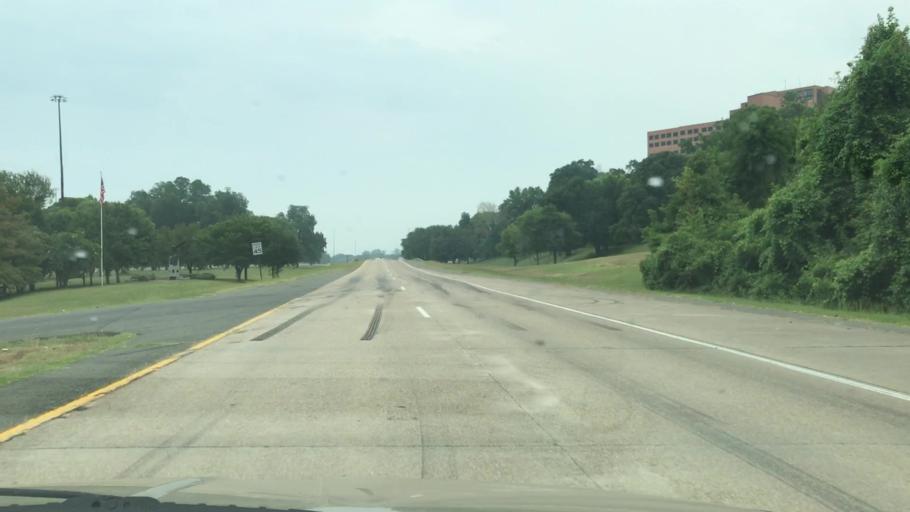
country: US
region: Louisiana
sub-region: Bossier Parish
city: Bossier City
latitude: 32.5059
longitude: -93.7232
